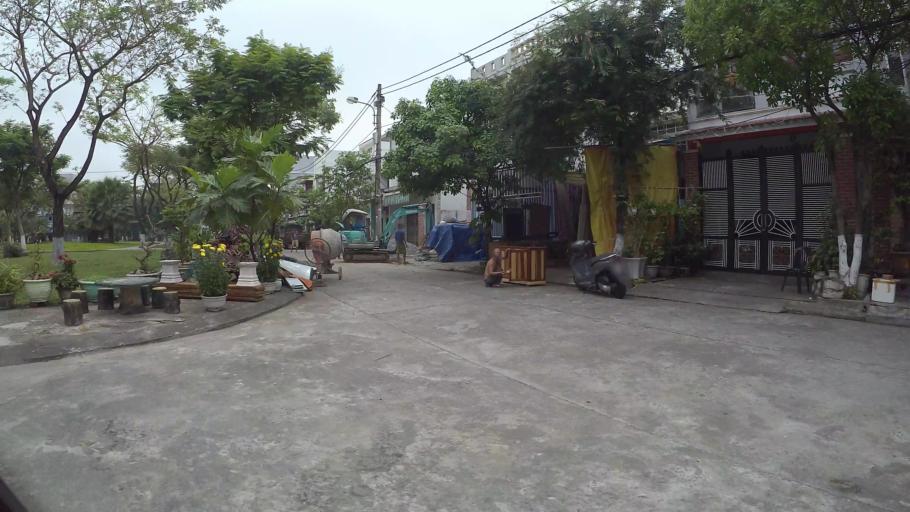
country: VN
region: Da Nang
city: Cam Le
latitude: 16.0276
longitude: 108.2121
